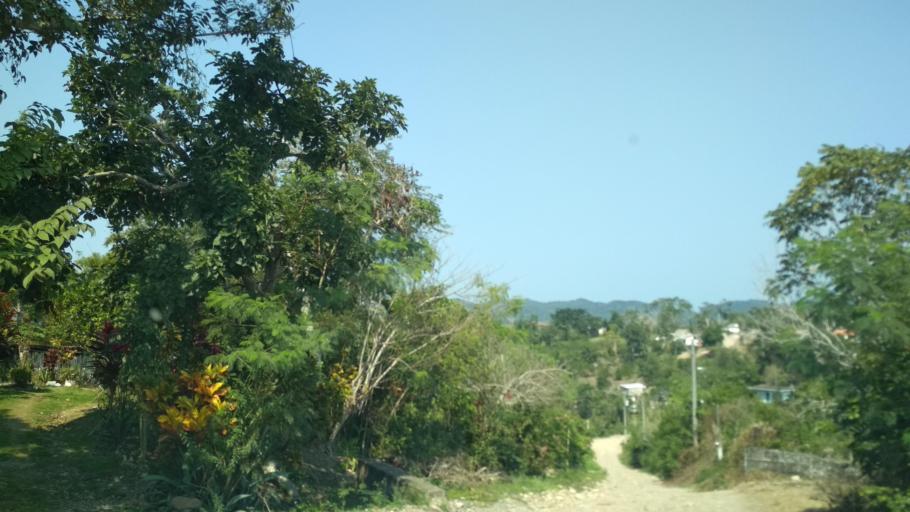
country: MX
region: Veracruz
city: Gutierrez Zamora
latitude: 20.4226
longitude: -97.1936
